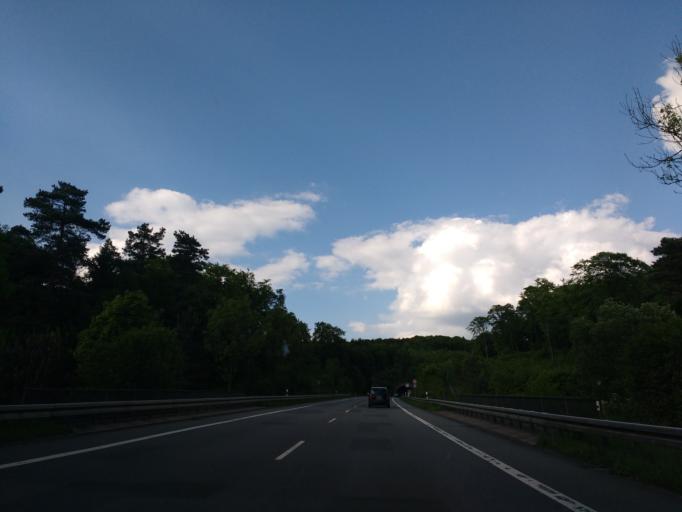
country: DE
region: North Rhine-Westphalia
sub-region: Regierungsbezirk Detmold
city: Oerlinghausen
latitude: 51.9512
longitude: 8.6469
